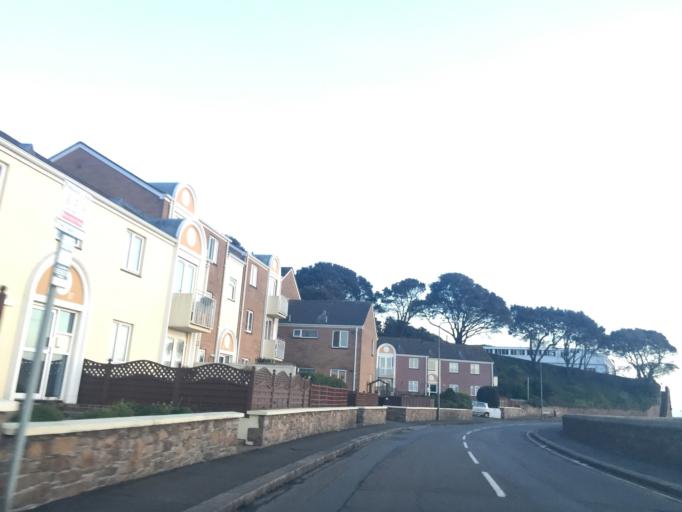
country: JE
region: St Helier
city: Saint Helier
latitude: 49.1790
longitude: -2.1085
